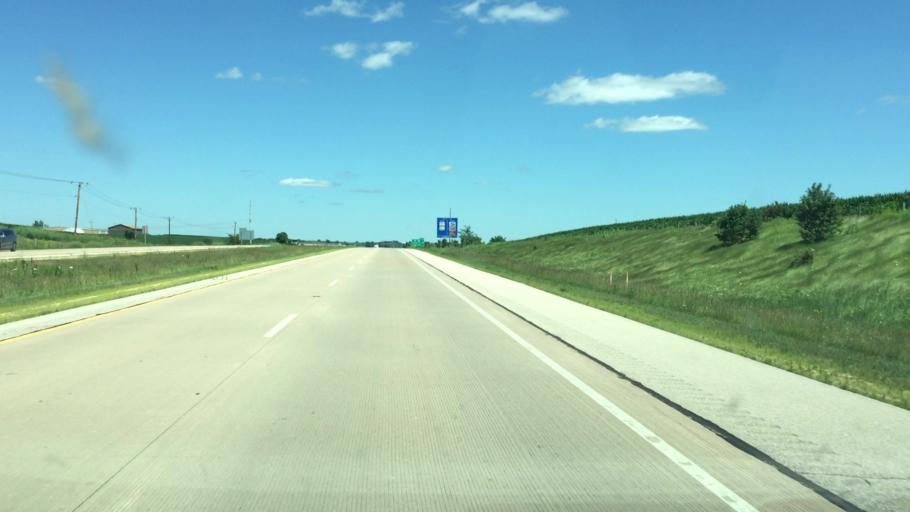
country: US
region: Wisconsin
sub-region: Grant County
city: Platteville
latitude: 42.7134
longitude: -90.4698
